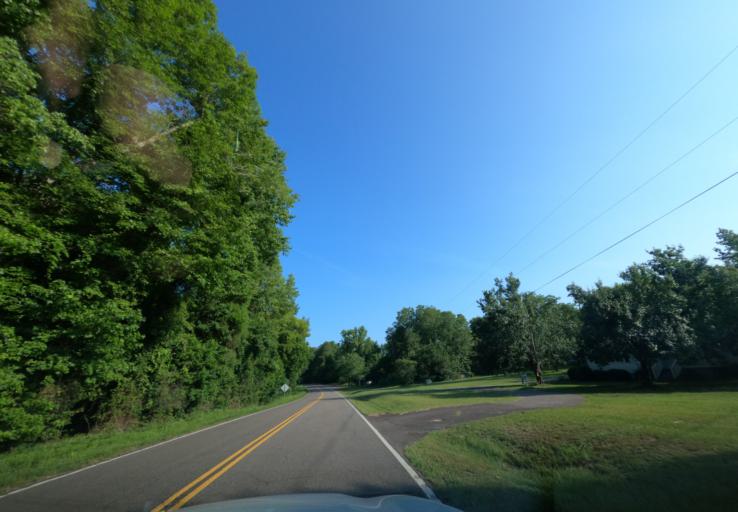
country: US
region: South Carolina
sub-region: Edgefield County
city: Murphys Estates
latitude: 33.6225
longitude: -81.9703
